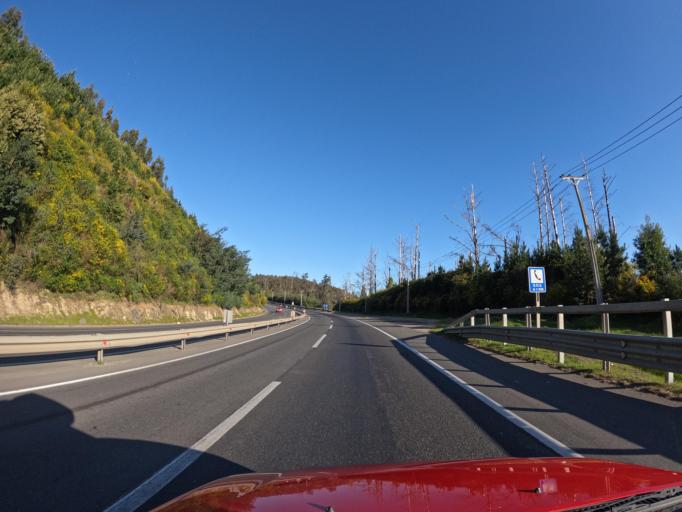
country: CL
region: Biobio
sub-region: Provincia de Concepcion
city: Penco
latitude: -36.7571
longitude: -72.9780
